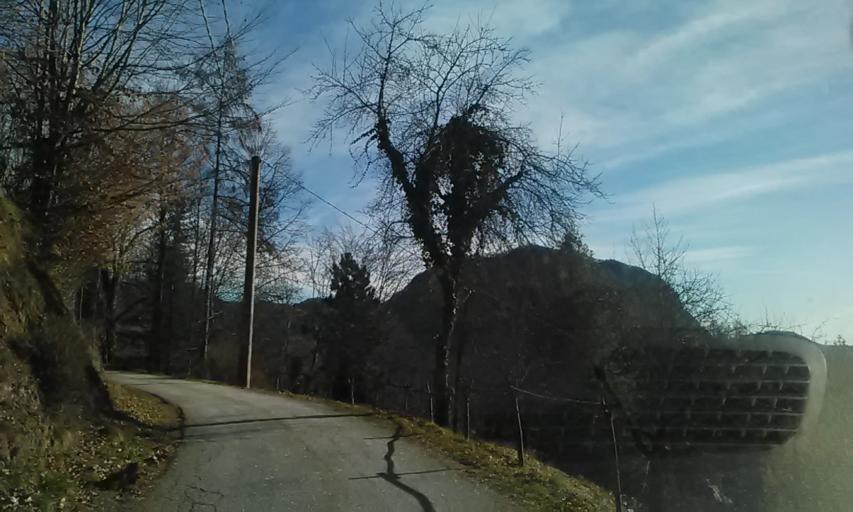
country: IT
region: Piedmont
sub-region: Provincia di Vercelli
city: Valduggia
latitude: 45.7362
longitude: 8.3130
